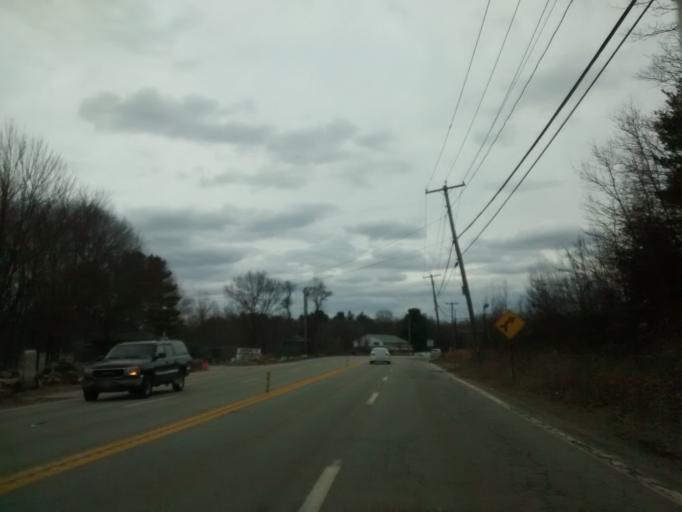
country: US
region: Massachusetts
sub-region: Worcester County
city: Auburn
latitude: 42.1702
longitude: -71.8835
